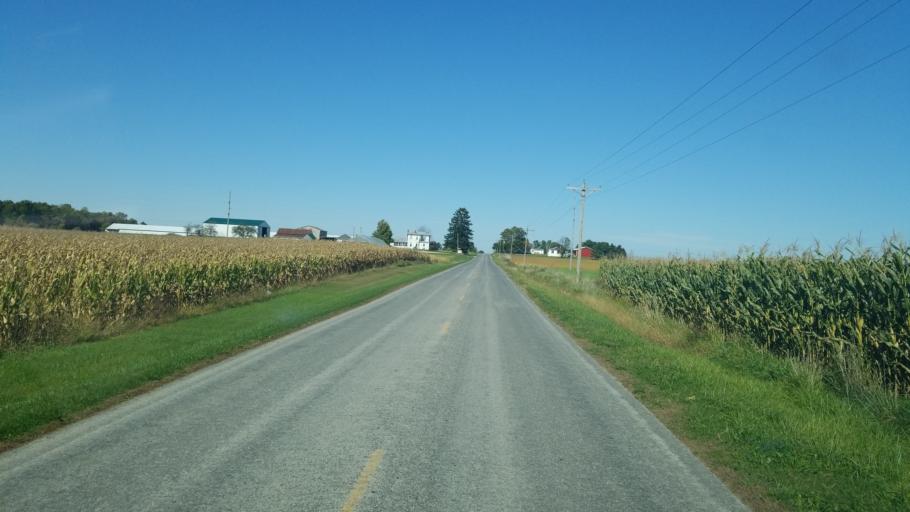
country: US
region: Ohio
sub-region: Huron County
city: Greenwich
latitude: 41.0335
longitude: -82.5844
